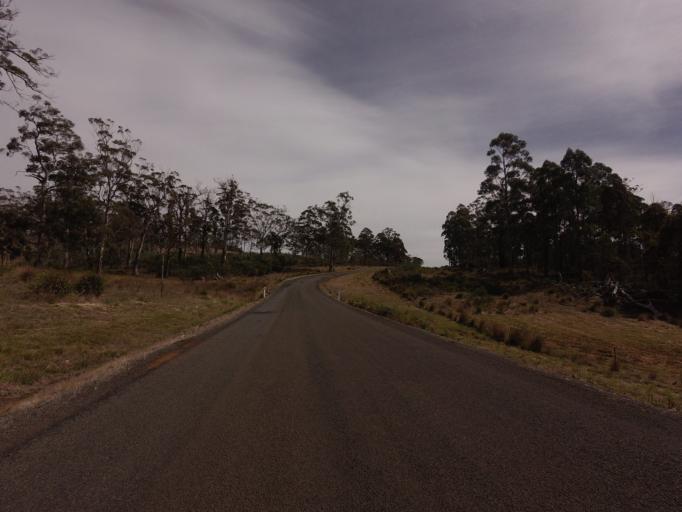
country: AU
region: Tasmania
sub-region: Sorell
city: Sorell
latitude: -42.5521
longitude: 147.6732
